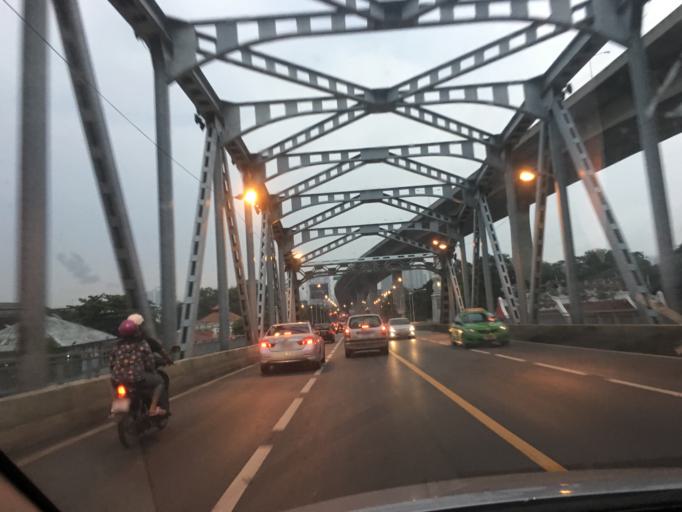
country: TH
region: Bangkok
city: Bang Kho Laem
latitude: 13.7015
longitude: 100.4911
